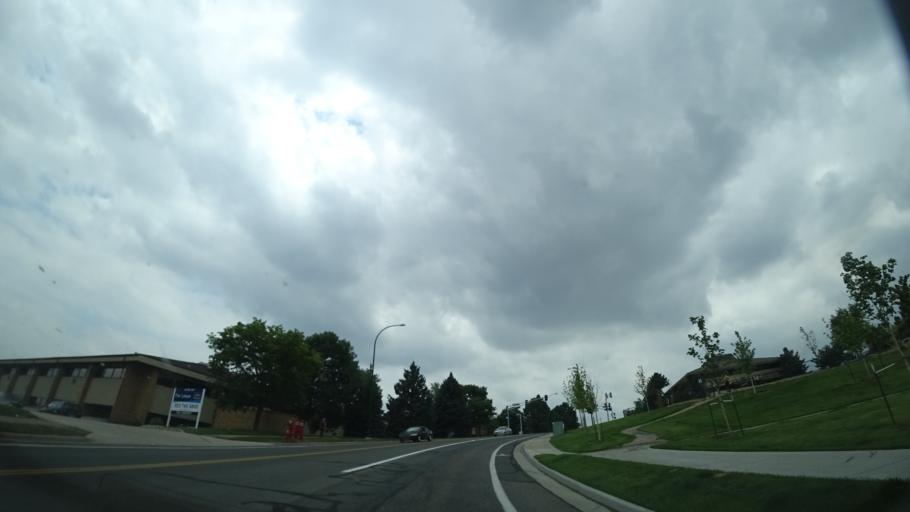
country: US
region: Colorado
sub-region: Jefferson County
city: West Pleasant View
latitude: 39.7145
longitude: -105.1379
